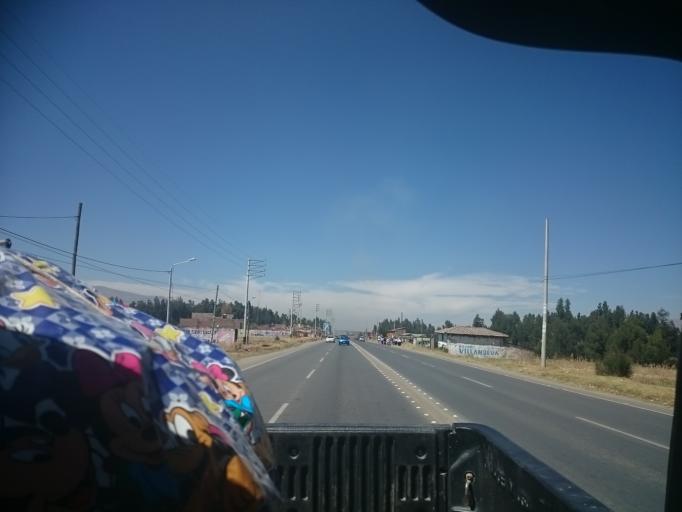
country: PE
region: Junin
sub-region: Provincia de Huancayo
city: San Agustin
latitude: -11.9667
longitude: -75.2711
